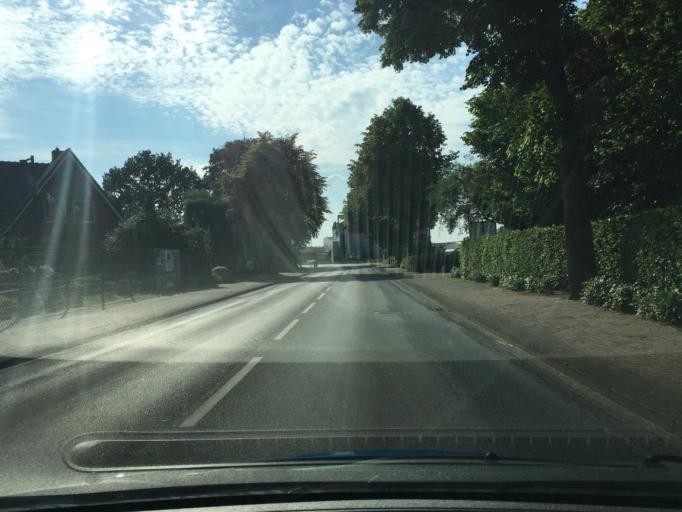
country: DE
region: Lower Saxony
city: Sittensen
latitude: 53.2800
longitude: 9.5005
